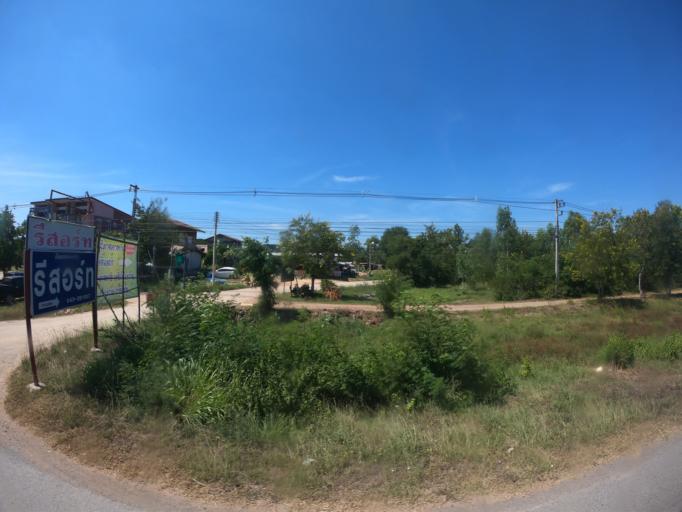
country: TH
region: Khon Kaen
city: Non Sila
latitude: 15.9685
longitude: 102.6919
